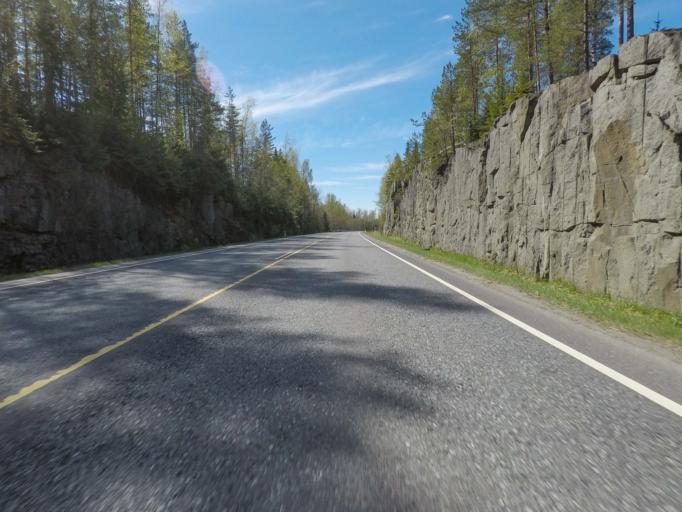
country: FI
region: Haeme
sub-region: Forssa
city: Humppila
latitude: 60.9820
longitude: 23.4408
